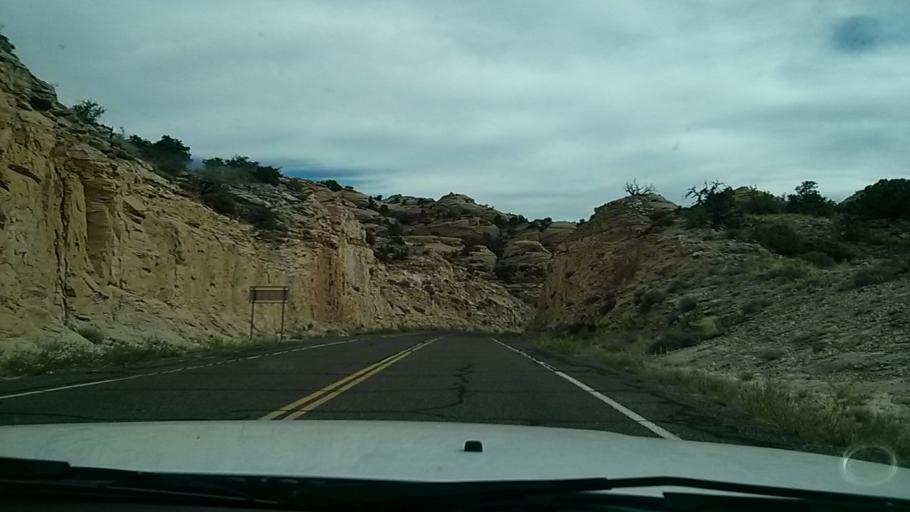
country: US
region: Utah
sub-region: Wayne County
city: Loa
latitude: 37.7997
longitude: -111.4069
